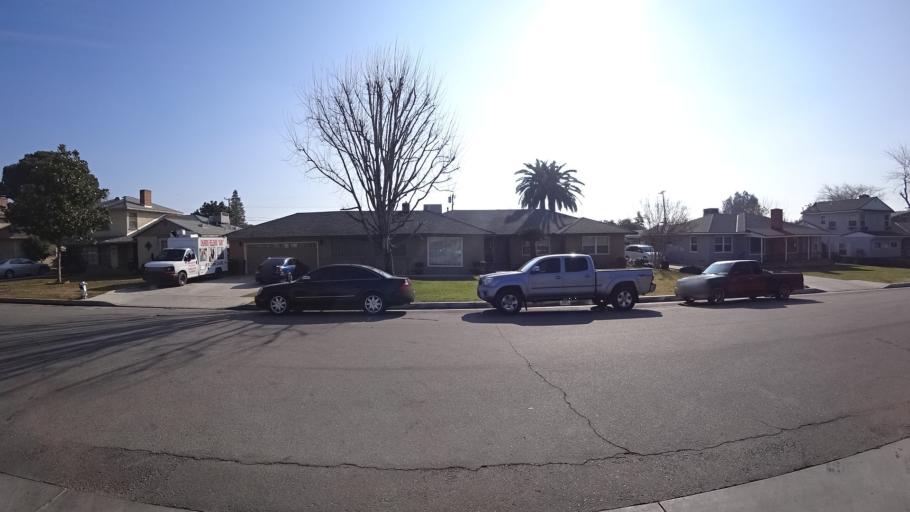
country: US
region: California
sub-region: Kern County
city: Bakersfield
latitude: 35.3965
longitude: -119.0006
